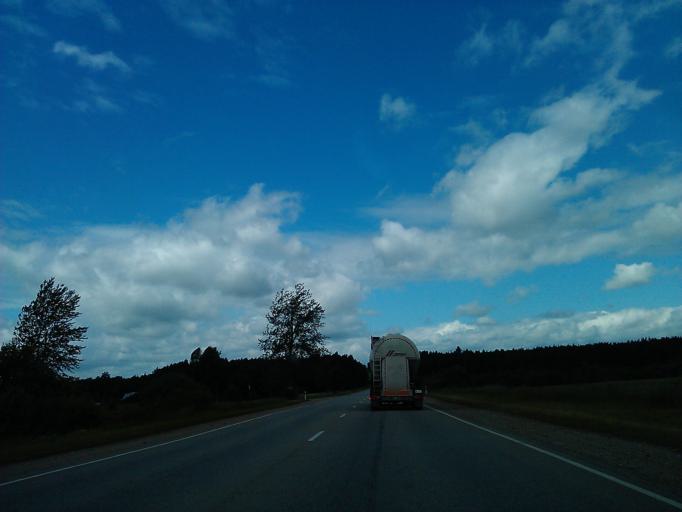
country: LV
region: Tukuma Rajons
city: Tukums
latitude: 56.9421
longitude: 23.1588
